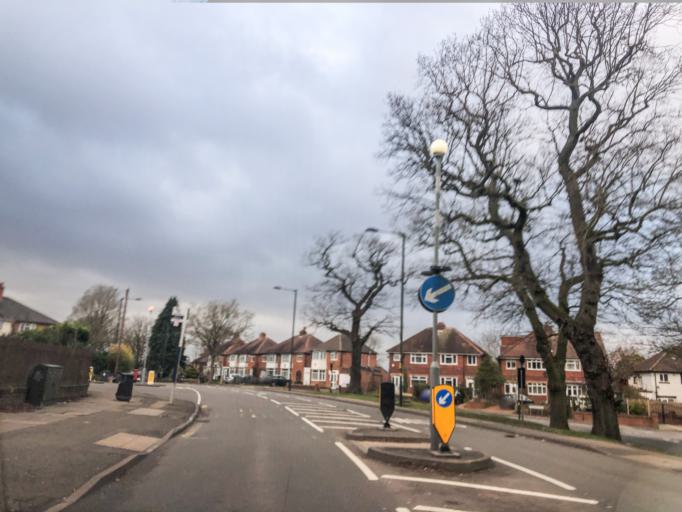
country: GB
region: England
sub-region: City and Borough of Birmingham
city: Birmingham
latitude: 52.4362
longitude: -1.9045
